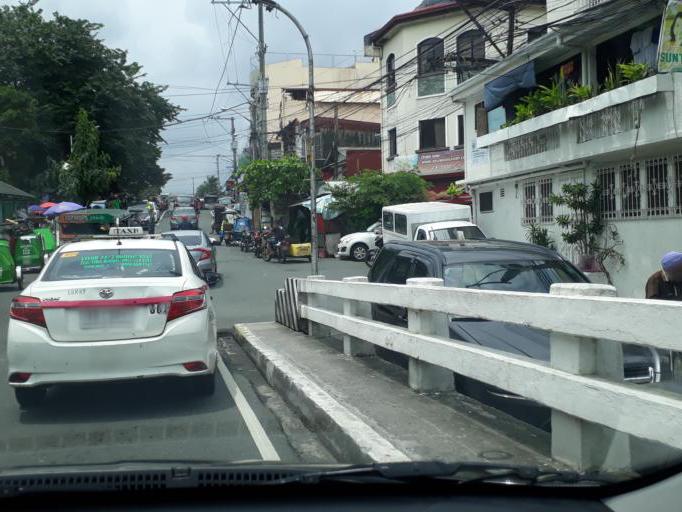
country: PH
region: Metro Manila
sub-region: San Juan
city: San Juan
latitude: 14.6251
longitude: 121.0373
